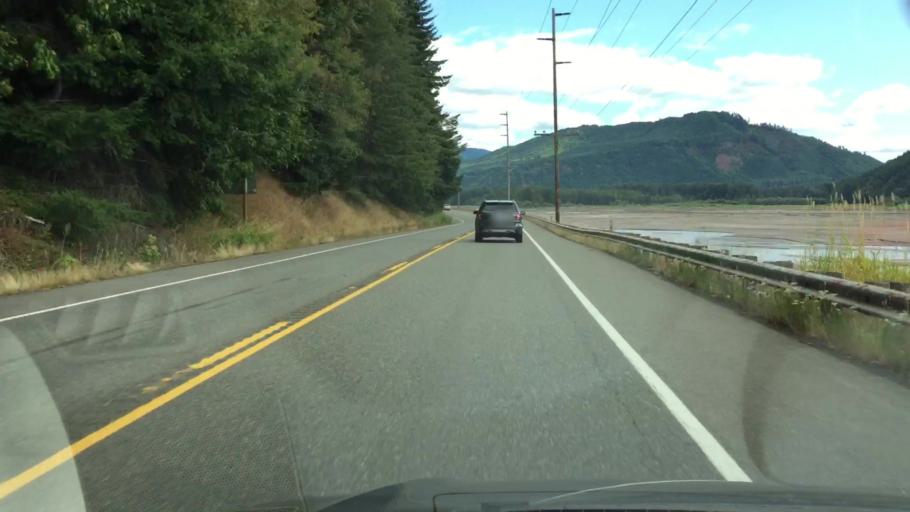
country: US
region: Washington
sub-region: Pierce County
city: Eatonville
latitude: 46.7730
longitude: -122.2162
